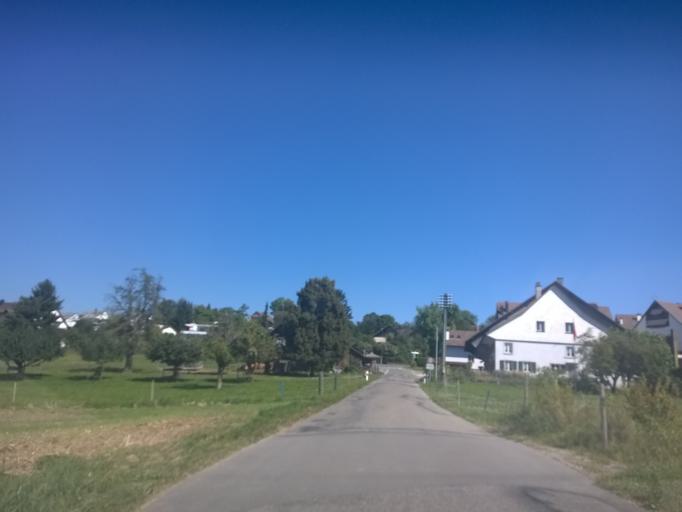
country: CH
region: Zurich
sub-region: Bezirk Buelach
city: Kloten / Hostrass
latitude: 47.4714
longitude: 8.6009
